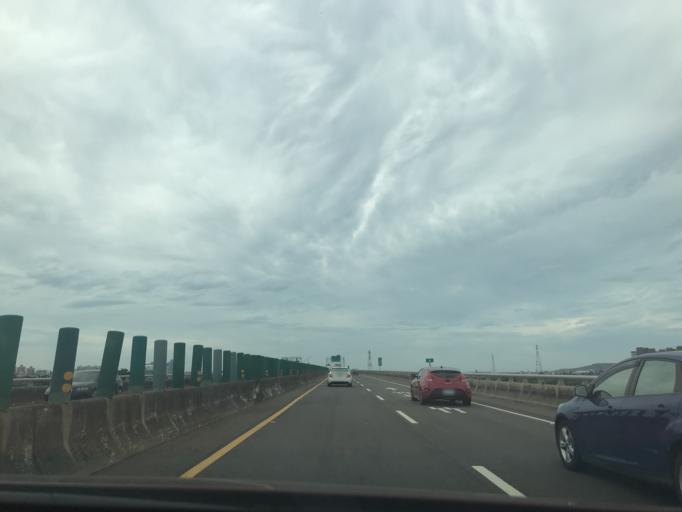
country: TW
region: Taiwan
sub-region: Hsinchu
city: Zhubei
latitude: 24.8148
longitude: 121.0043
